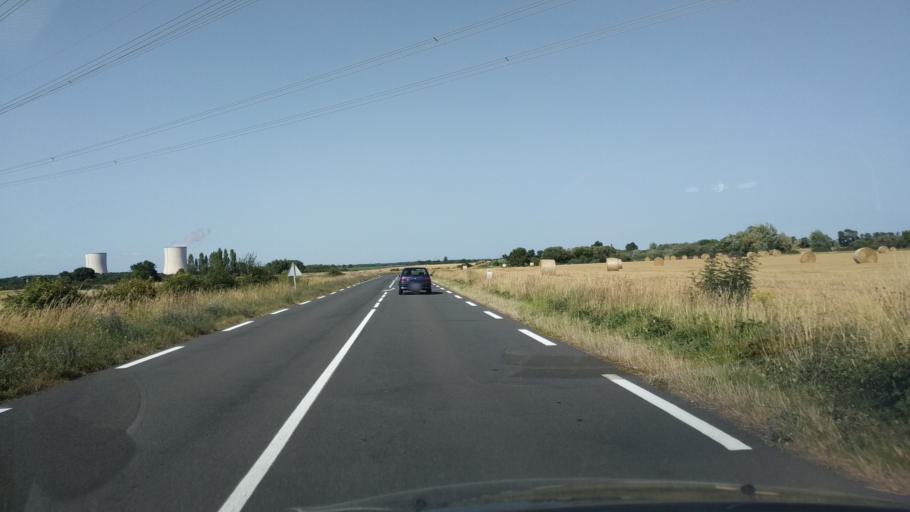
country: FR
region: Poitou-Charentes
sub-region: Departement de la Vienne
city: Lussac-les-Chateaux
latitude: 46.4271
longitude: 0.6391
